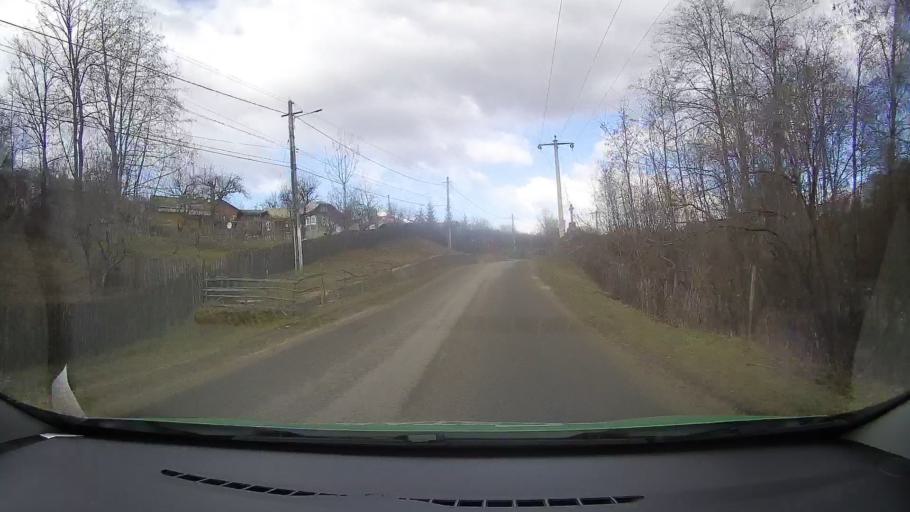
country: RO
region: Dambovita
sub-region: Comuna Buciumeni
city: Buciumeni
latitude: 45.1309
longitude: 25.4682
